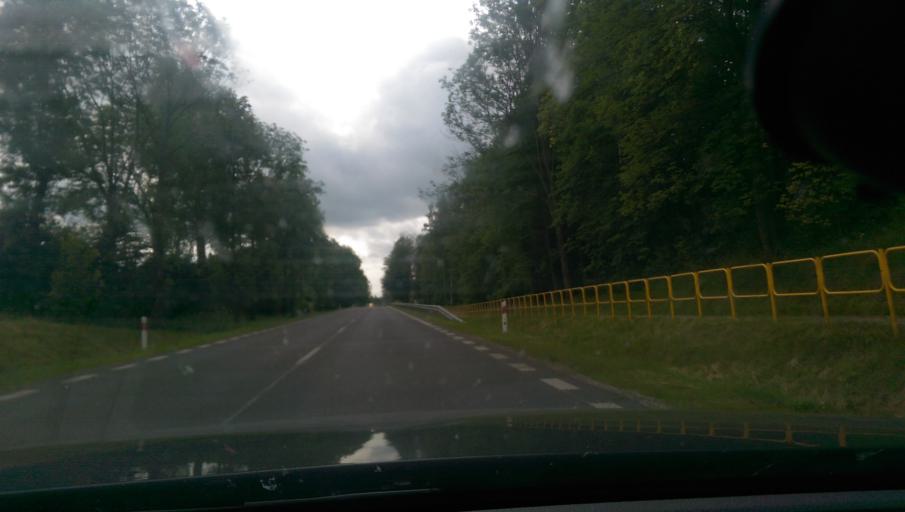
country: PL
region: Warmian-Masurian Voivodeship
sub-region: Powiat goldapski
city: Goldap
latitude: 54.2913
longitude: 22.3247
